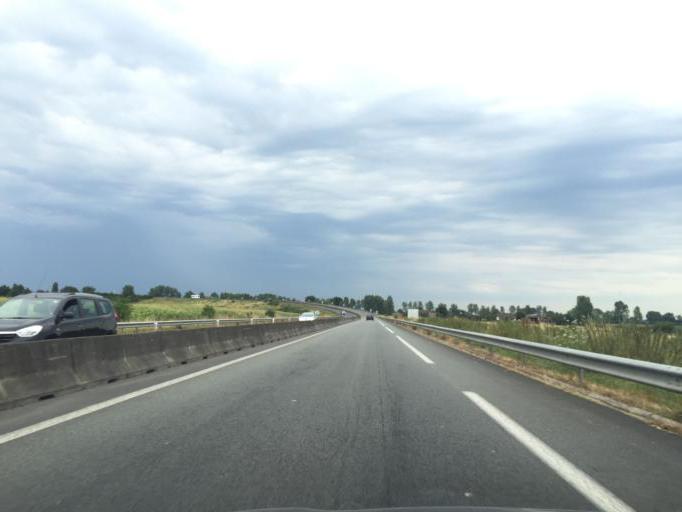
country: FR
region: Auvergne
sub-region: Departement de l'Allier
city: Toulon-sur-Allier
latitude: 46.5057
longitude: 3.3567
